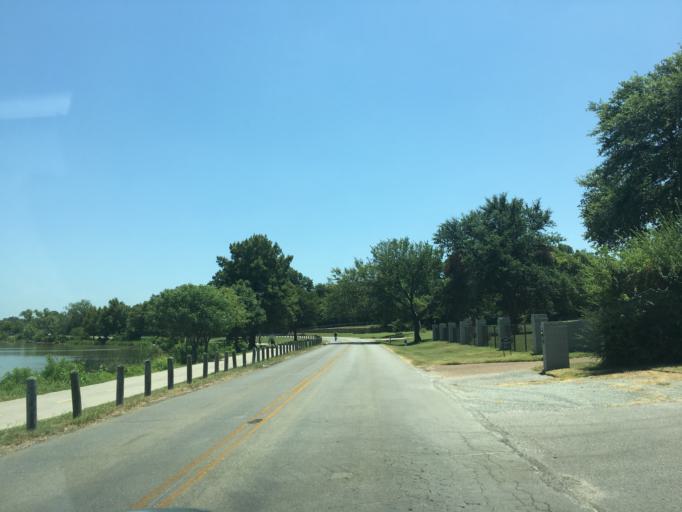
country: US
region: Texas
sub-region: Dallas County
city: Highland Park
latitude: 32.8386
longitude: -96.7281
